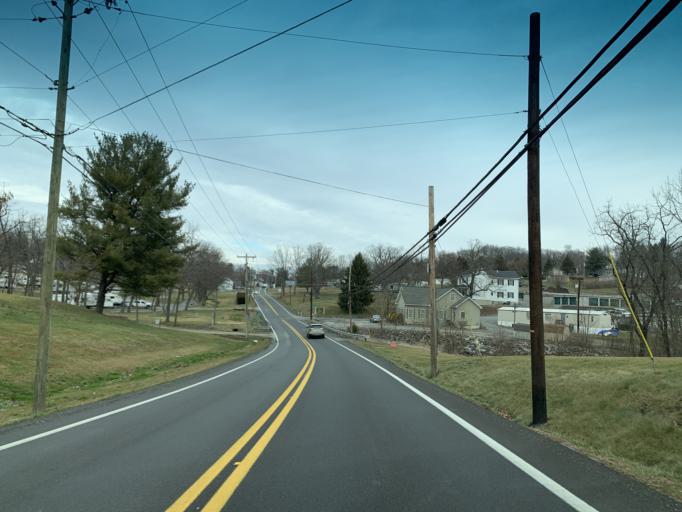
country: US
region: Maryland
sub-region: Washington County
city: Williamsport
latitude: 39.5660
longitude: -77.8833
